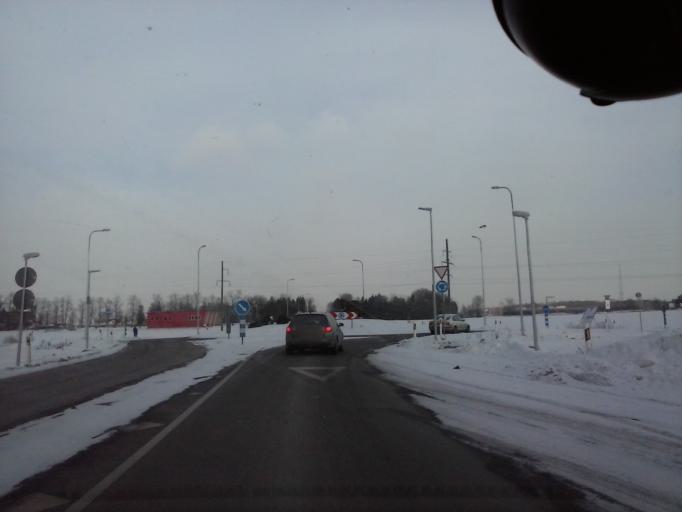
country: EE
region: Tartu
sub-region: Tartu linn
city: Tartu
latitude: 58.3620
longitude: 26.6593
